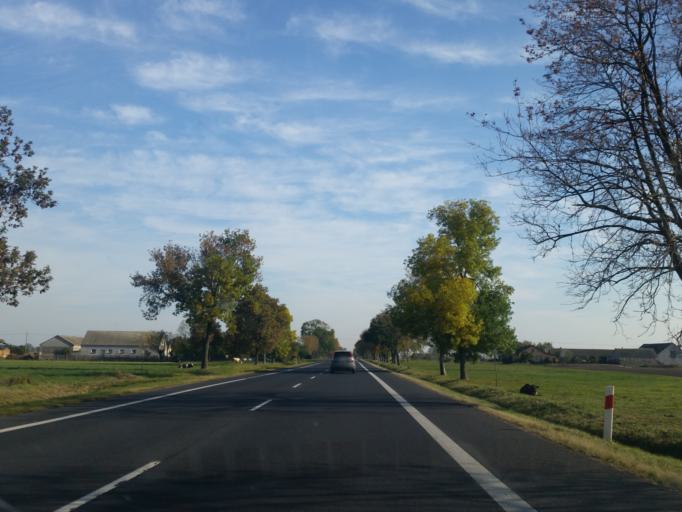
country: PL
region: Masovian Voivodeship
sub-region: Powiat plocki
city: Drobin
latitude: 52.7632
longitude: 19.9448
